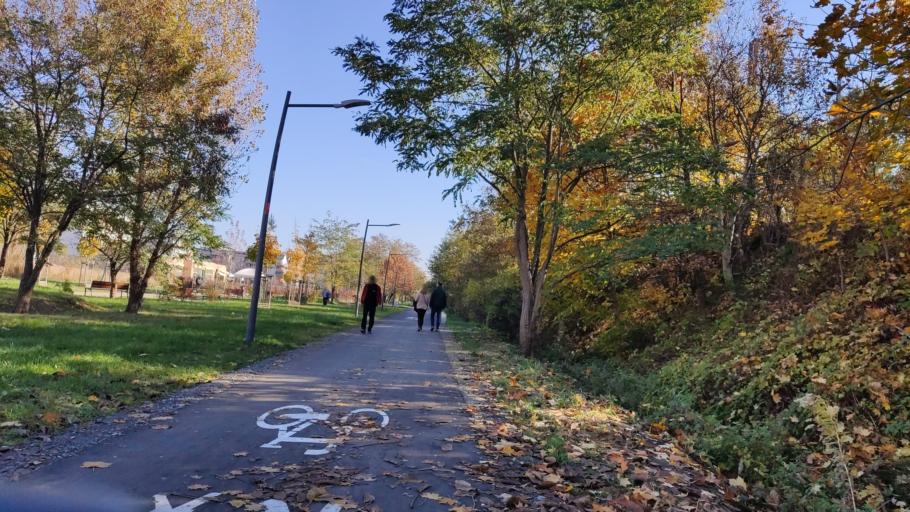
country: PL
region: Lower Silesian Voivodeship
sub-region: Powiat wroclawski
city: Wroclaw
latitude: 51.0713
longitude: 17.0400
